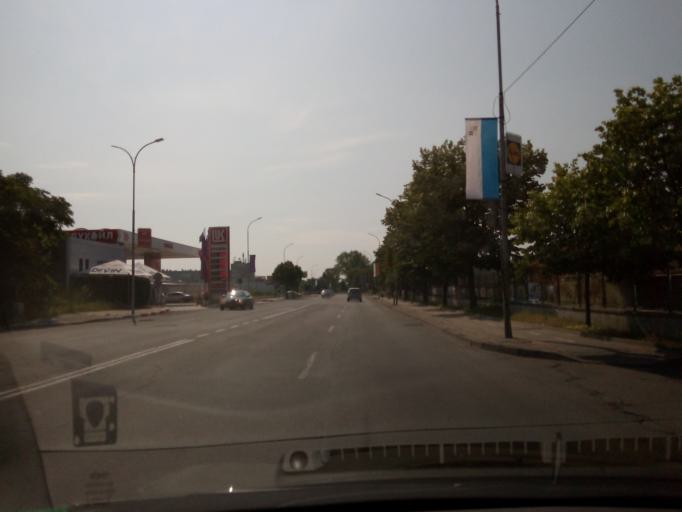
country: BG
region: Burgas
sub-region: Obshtina Pomorie
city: Pomorie
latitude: 42.5667
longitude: 27.6201
